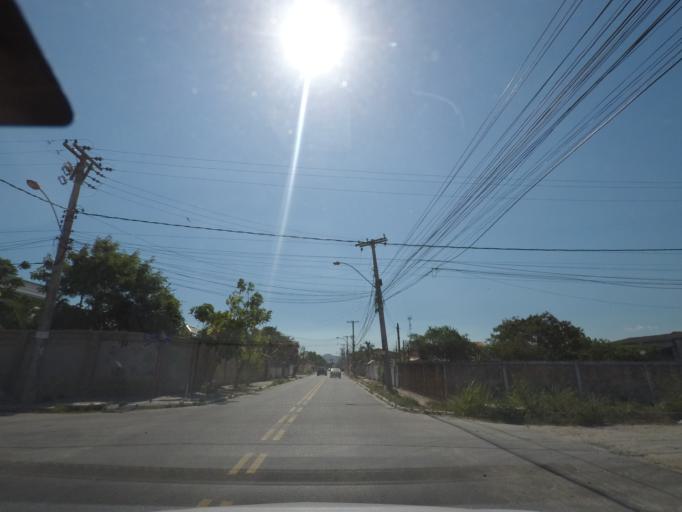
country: BR
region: Rio de Janeiro
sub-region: Marica
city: Marica
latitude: -22.9670
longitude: -42.9405
